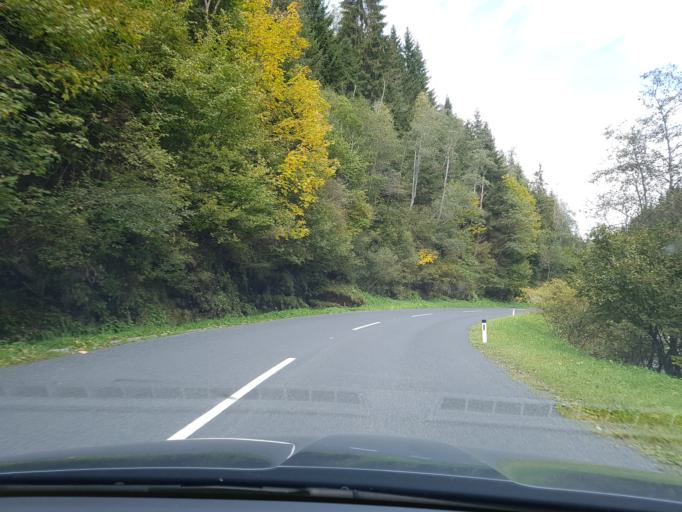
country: AT
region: Styria
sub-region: Politischer Bezirk Murau
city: Stadl an der Mur
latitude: 47.0424
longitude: 13.9051
